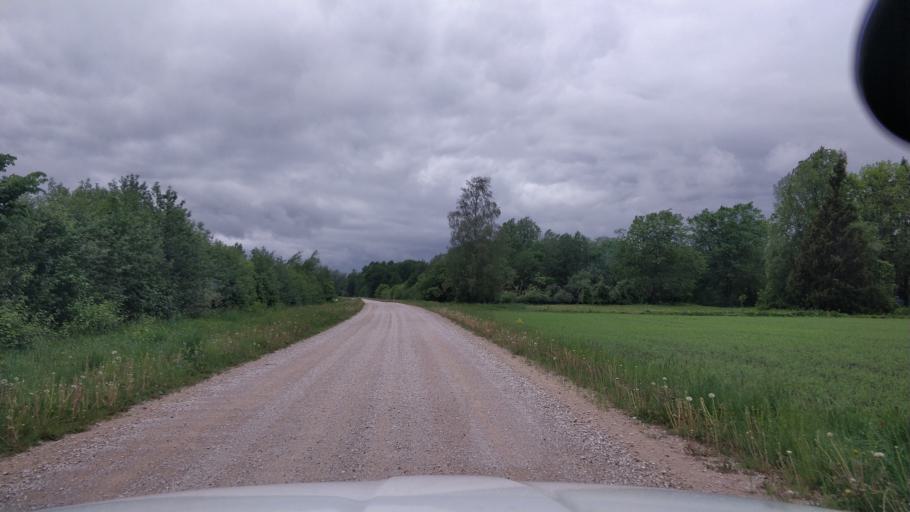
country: EE
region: Paernumaa
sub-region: Halinga vald
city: Parnu-Jaagupi
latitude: 58.7092
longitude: 24.3341
